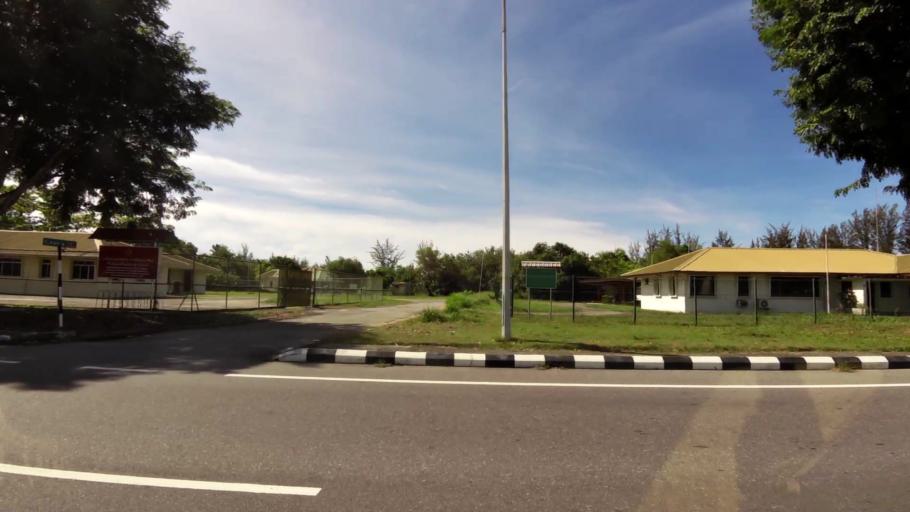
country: BN
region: Belait
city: Kuala Belait
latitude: 4.5889
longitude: 114.2049
